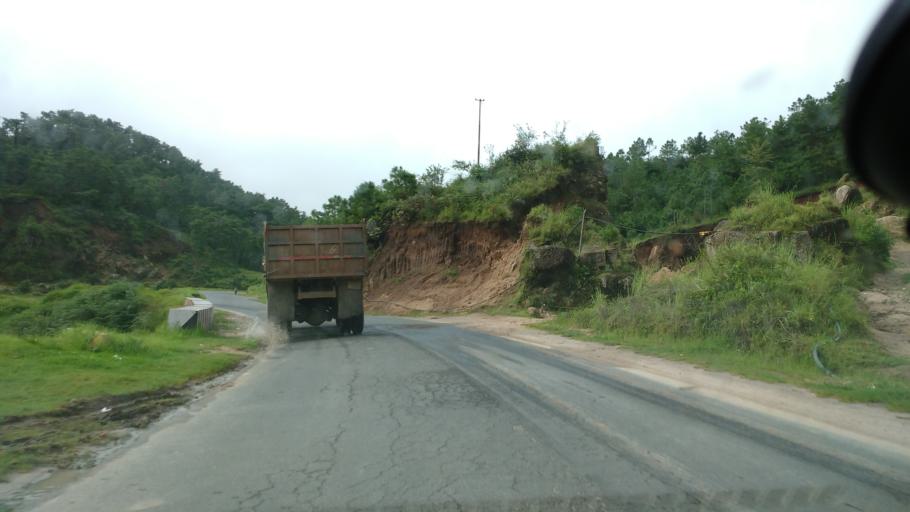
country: IN
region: Meghalaya
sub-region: East Khasi Hills
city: Shillong
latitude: 25.4794
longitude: 91.8199
